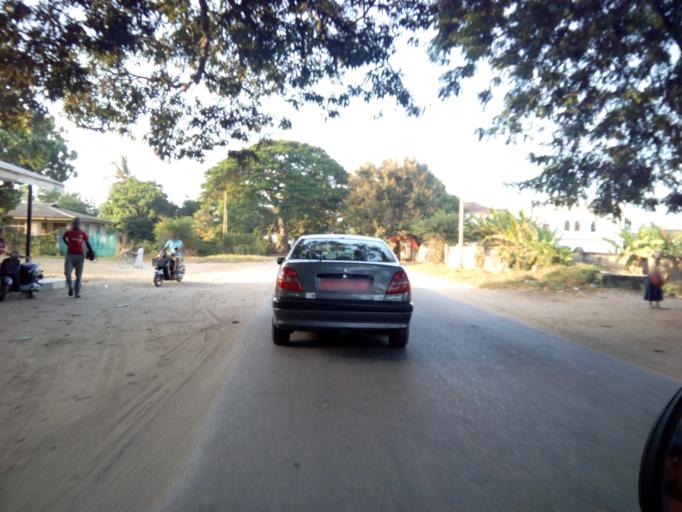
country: TZ
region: Zanzibar Urban/West
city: Zanzibar
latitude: -6.2060
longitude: 39.2100
